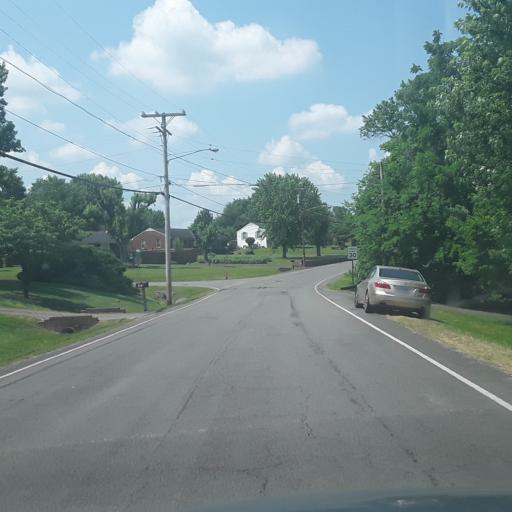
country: US
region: Tennessee
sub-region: Williamson County
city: Brentwood Estates
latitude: 36.0541
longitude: -86.7102
